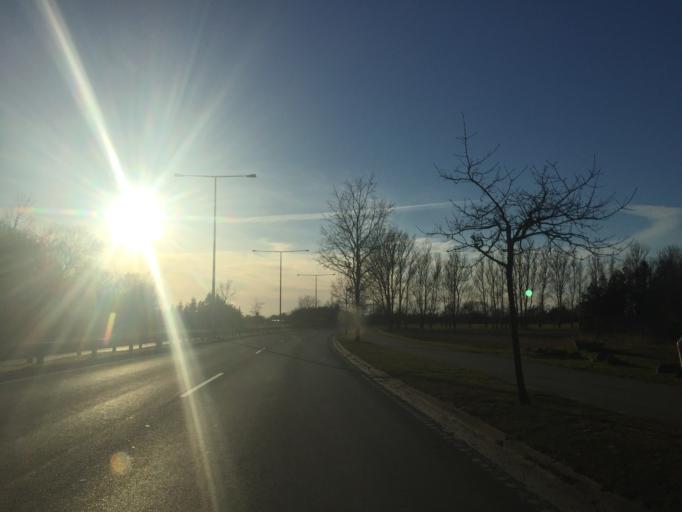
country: DK
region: Capital Region
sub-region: Dragor Kommune
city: Dragor
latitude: 55.5964
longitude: 12.6316
